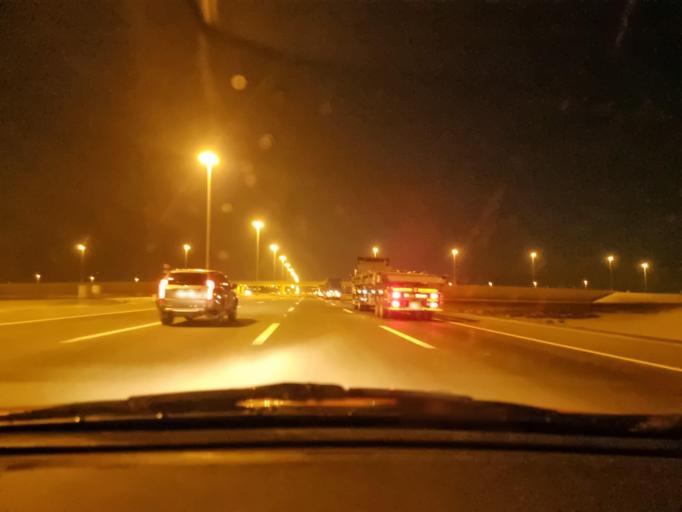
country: AE
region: Abu Dhabi
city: Abu Dhabi
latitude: 24.5595
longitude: 54.7474
